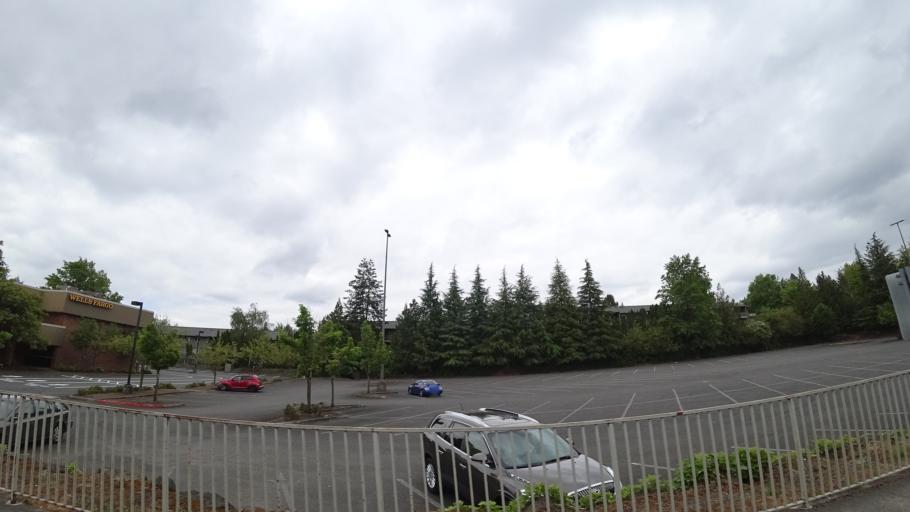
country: US
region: Oregon
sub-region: Washington County
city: Metzger
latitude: 45.4533
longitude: -122.7816
